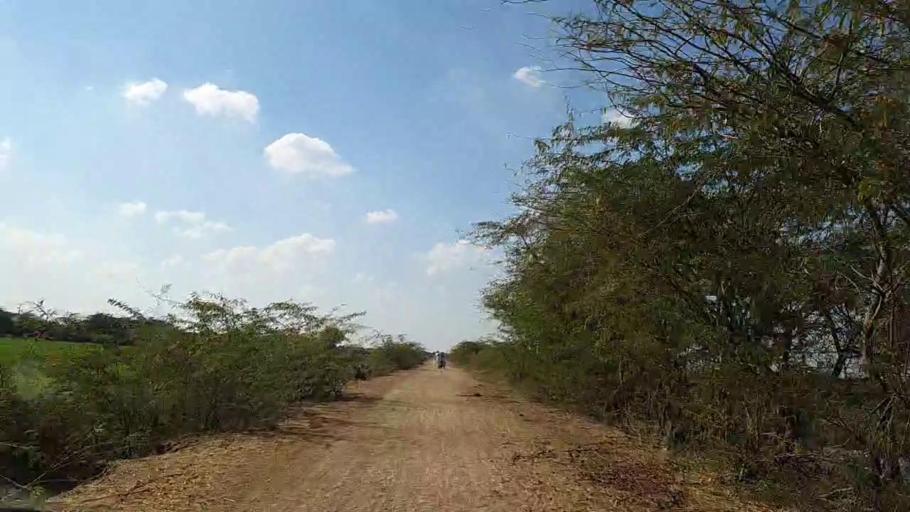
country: PK
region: Sindh
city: Pithoro
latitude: 25.6141
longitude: 69.4077
